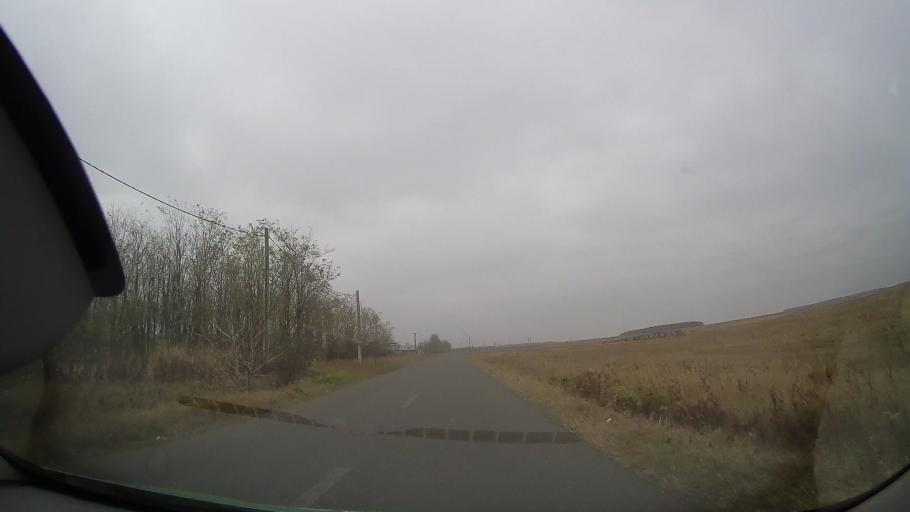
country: RO
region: Buzau
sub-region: Comuna Scutelnici
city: Scutelnici
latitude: 44.8525
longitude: 26.9103
